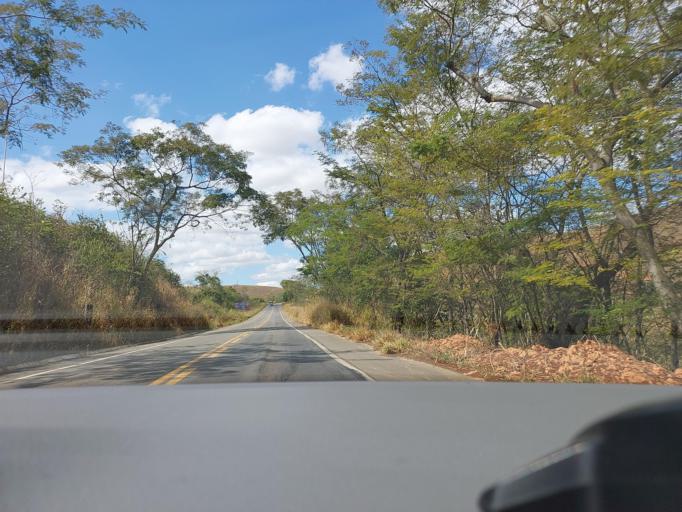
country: BR
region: Minas Gerais
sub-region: Muriae
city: Muriae
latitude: -21.1491
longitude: -42.1562
